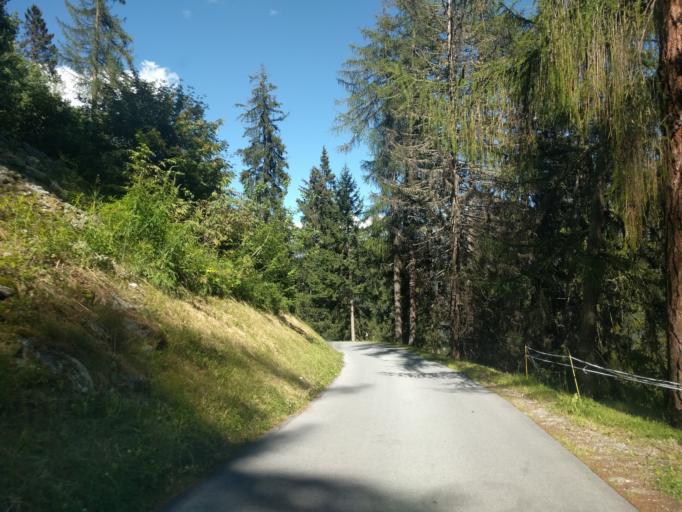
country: IT
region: Trentino-Alto Adige
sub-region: Bolzano
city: Tubre
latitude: 46.6082
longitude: 10.4158
